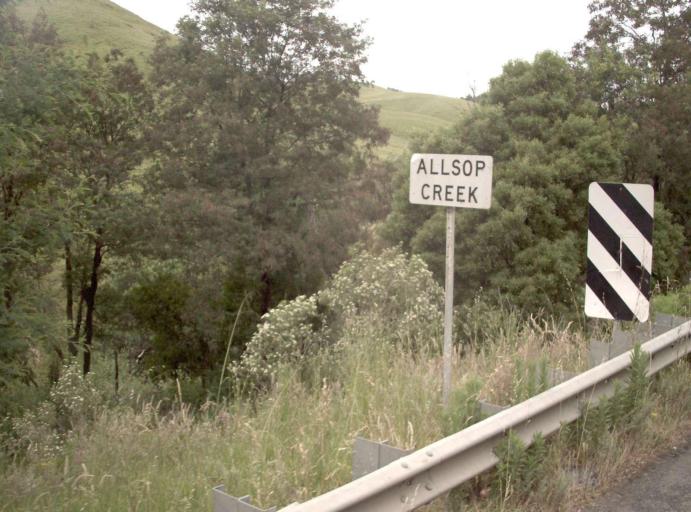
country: AU
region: Victoria
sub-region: Bass Coast
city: North Wonthaggi
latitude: -38.3734
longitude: 145.7186
